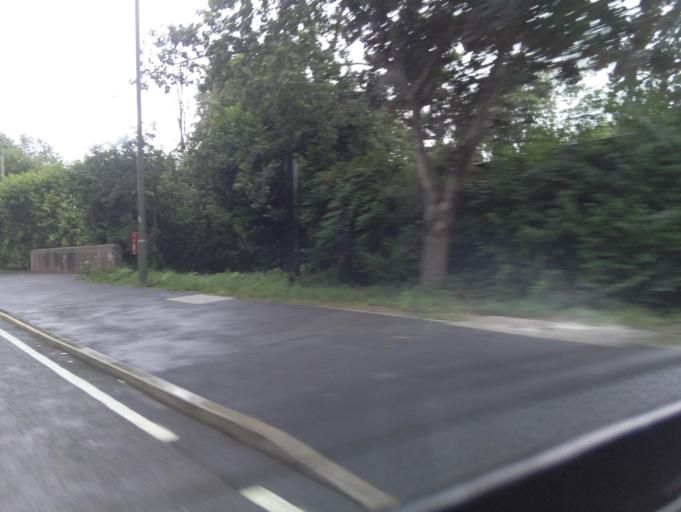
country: GB
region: England
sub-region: Surrey
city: Horley
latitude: 51.1869
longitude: -0.1638
